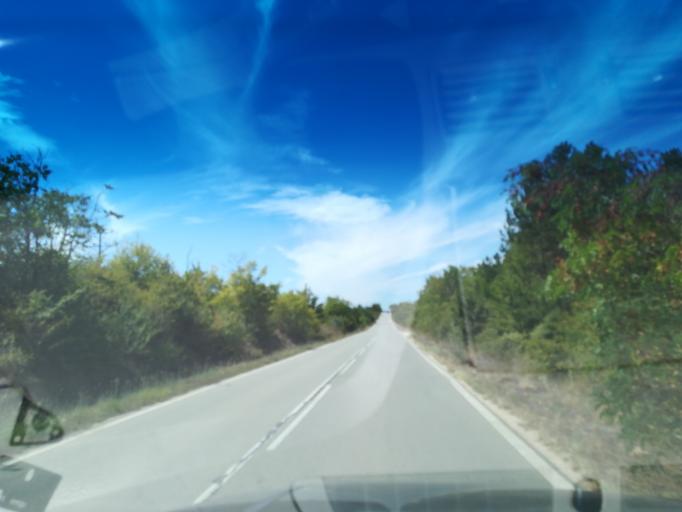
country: BG
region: Plovdiv
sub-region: Obshtina Suedinenie
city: Suedinenie
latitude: 42.3980
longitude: 24.5551
